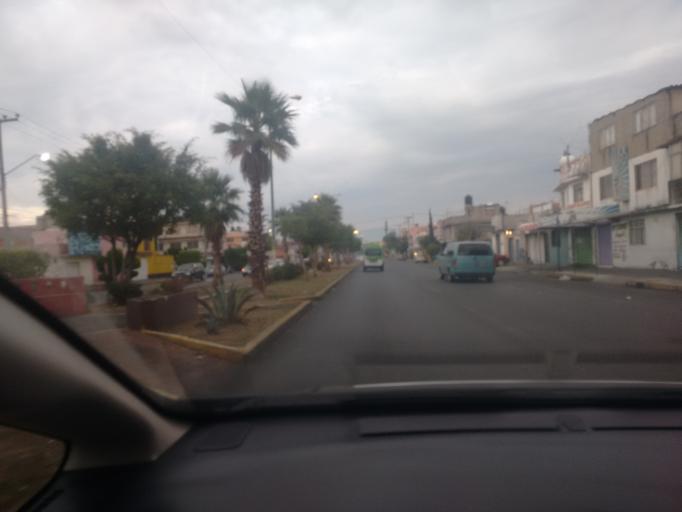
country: MX
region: Mexico City
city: Gustavo A. Madero
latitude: 19.4865
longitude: -99.0536
